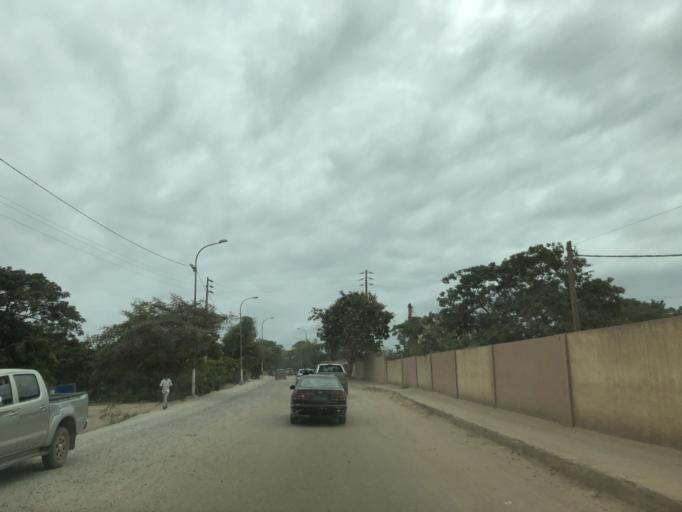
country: AO
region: Cuanza Sul
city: Sumbe
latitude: -11.1996
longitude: 13.8460
